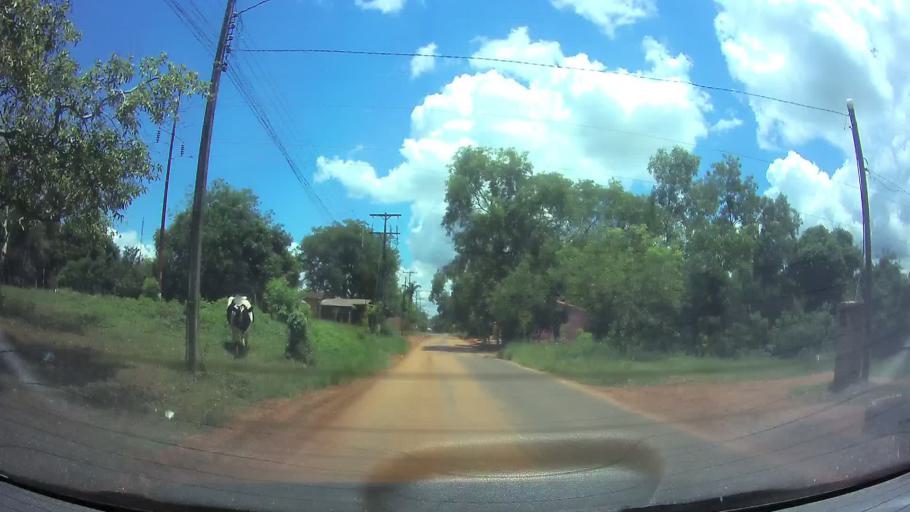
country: PY
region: Central
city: Itaugua
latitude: -25.3794
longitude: -57.3662
